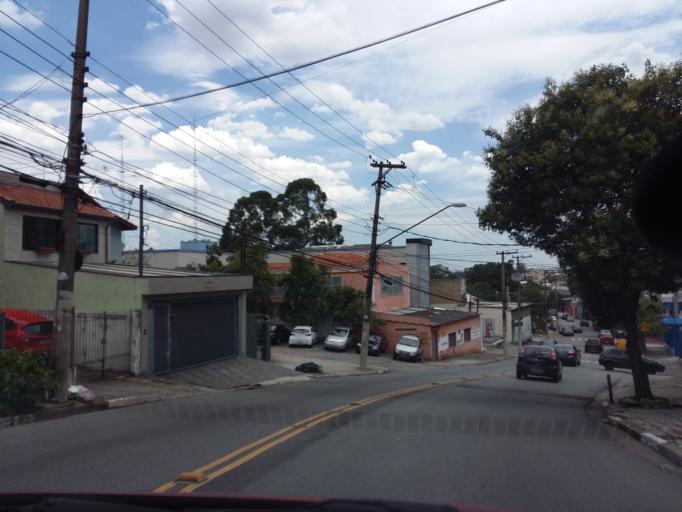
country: BR
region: Sao Paulo
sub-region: Sao Caetano Do Sul
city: Sao Caetano do Sul
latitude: -23.6308
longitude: -46.6012
